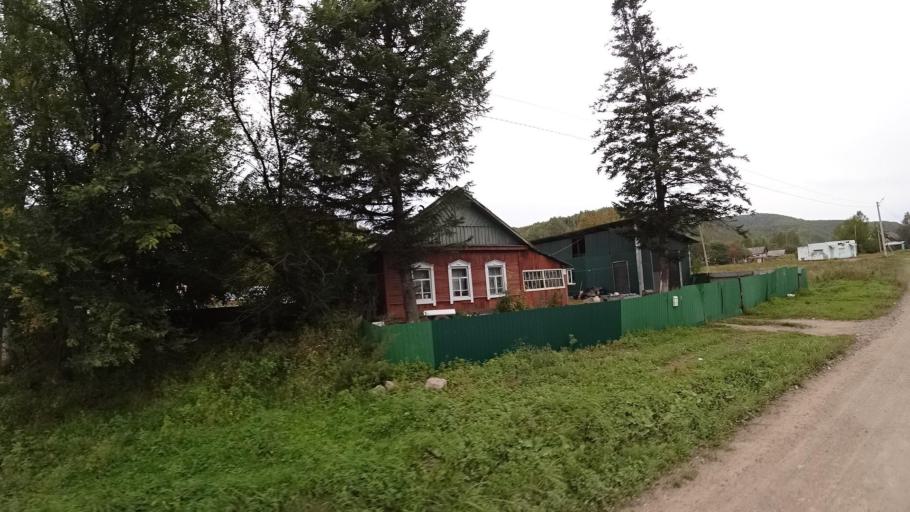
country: RU
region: Jewish Autonomous Oblast
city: Khingansk
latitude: 49.0230
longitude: 131.0482
